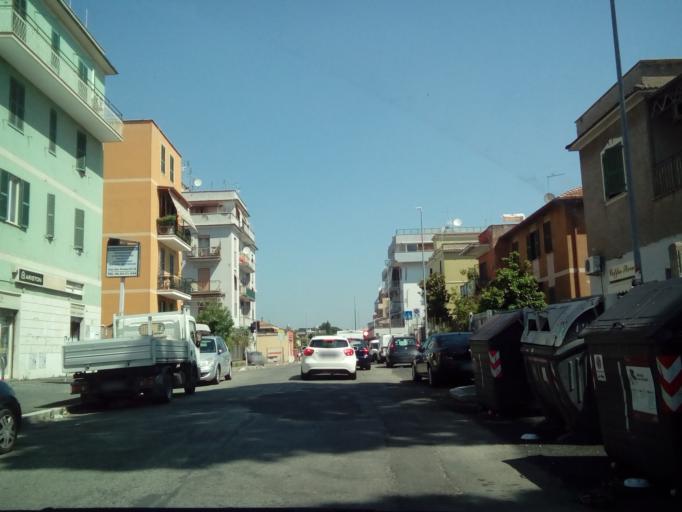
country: IT
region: Latium
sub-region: Citta metropolitana di Roma Capitale
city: Rome
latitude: 41.8820
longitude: 12.5773
